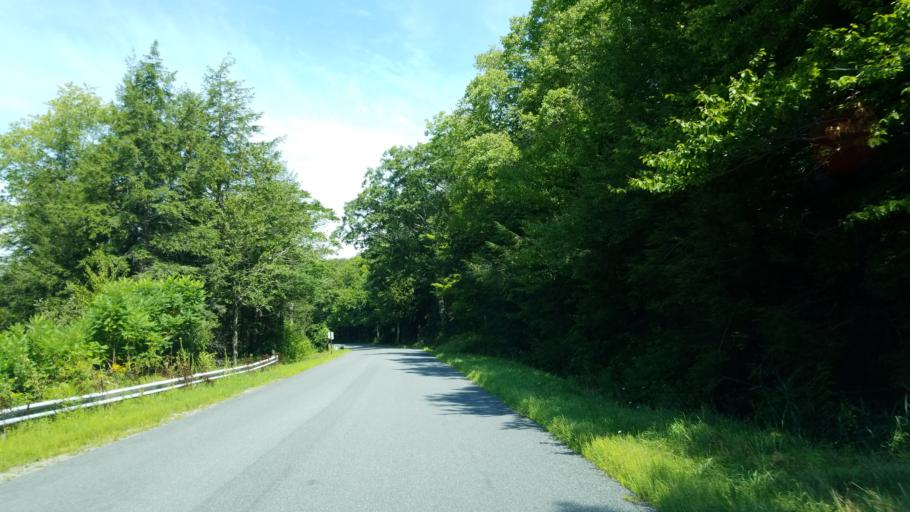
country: US
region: Connecticut
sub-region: Litchfield County
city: Winchester Center
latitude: 41.8951
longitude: -73.2116
